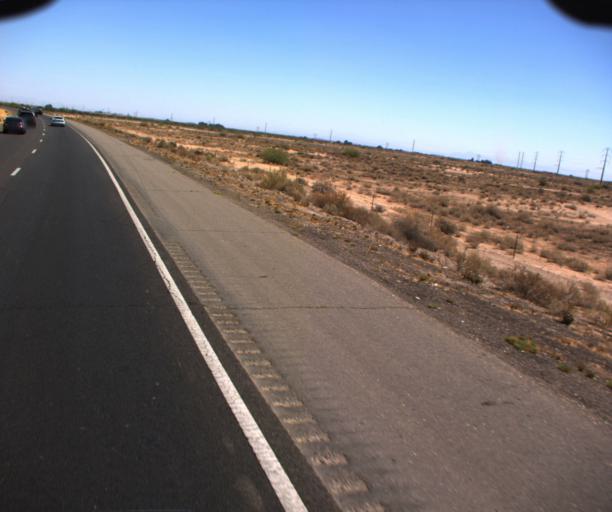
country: US
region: Arizona
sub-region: Pinal County
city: Maricopa
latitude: 33.1411
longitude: -112.0082
